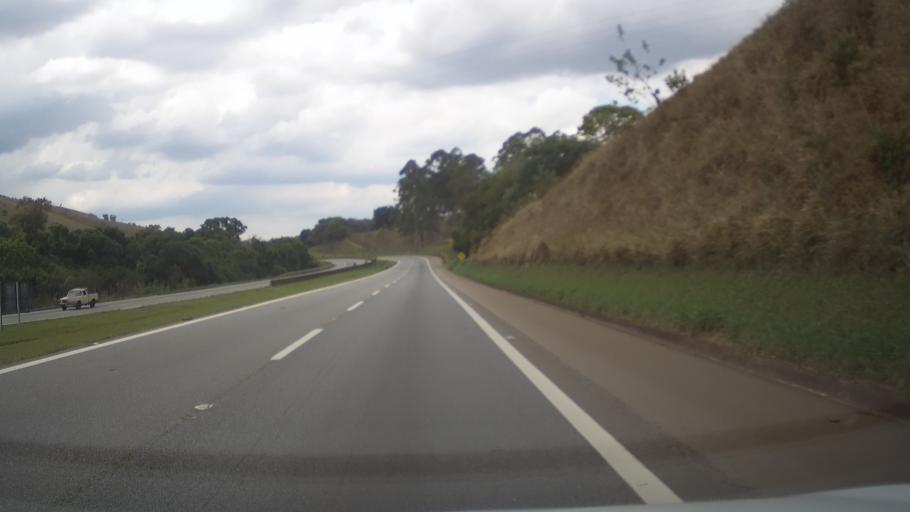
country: BR
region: Minas Gerais
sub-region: Tres Coracoes
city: Tres Coracoes
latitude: -21.5245
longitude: -45.2255
